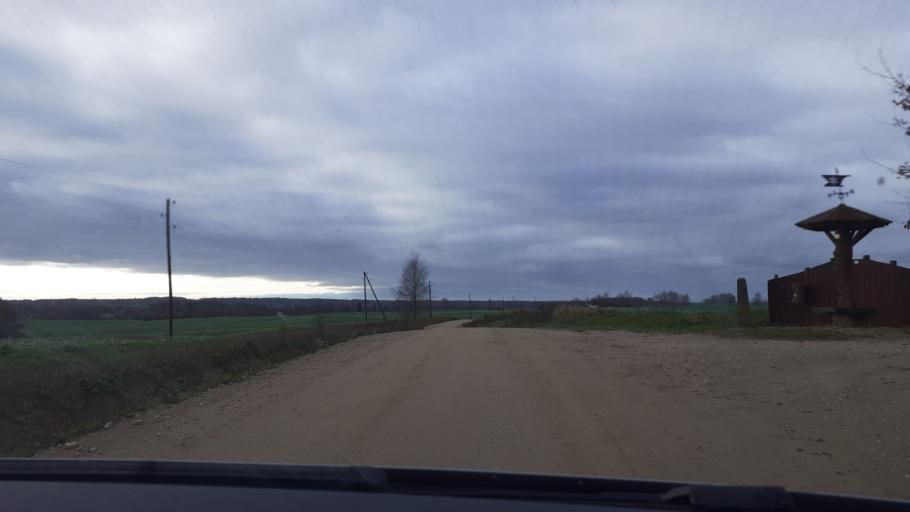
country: LV
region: Aizpute
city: Aizpute
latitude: 56.7697
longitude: 21.8071
